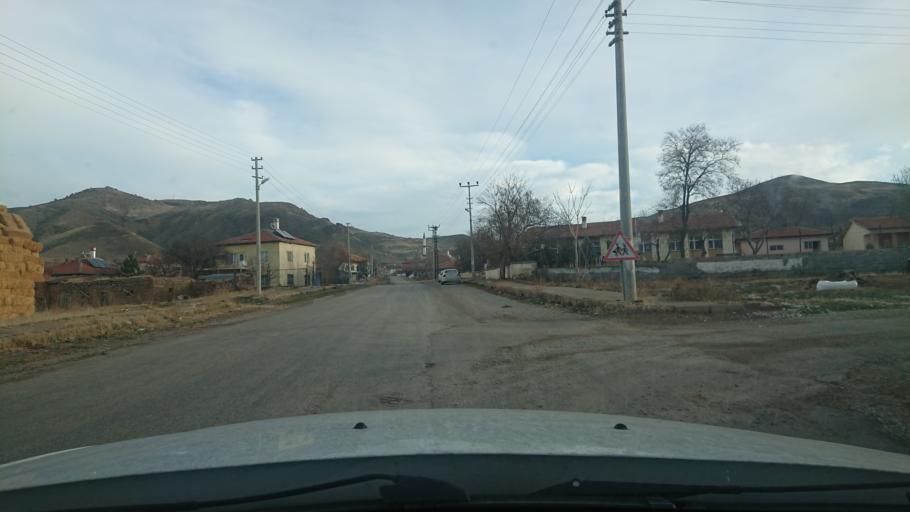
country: TR
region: Aksaray
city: Acipinar
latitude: 38.6152
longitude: 33.7824
